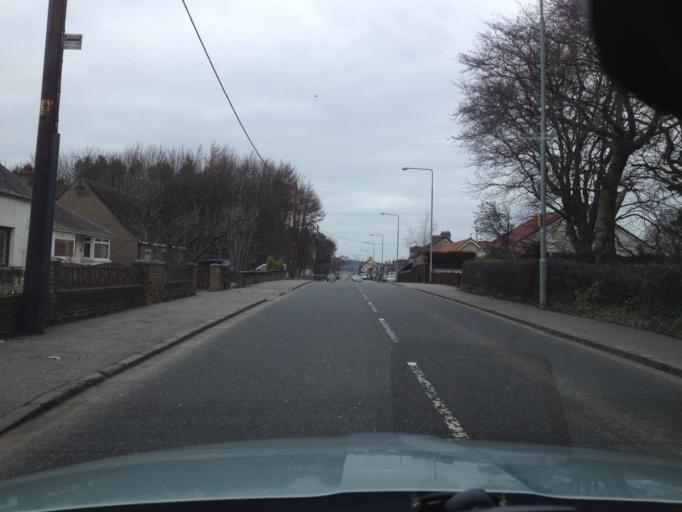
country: GB
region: Scotland
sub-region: West Lothian
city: Livingston
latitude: 55.9125
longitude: -3.4988
